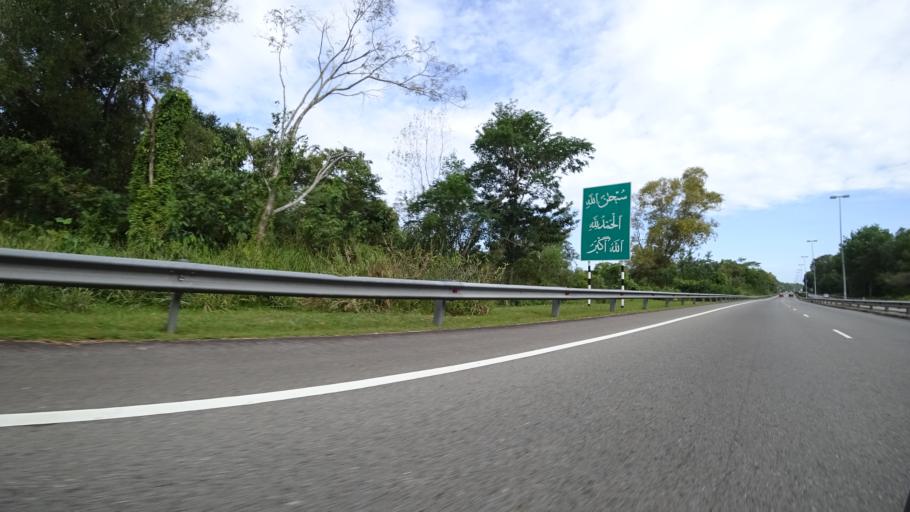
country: BN
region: Brunei and Muara
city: Bandar Seri Begawan
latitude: 4.9301
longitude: 114.9117
